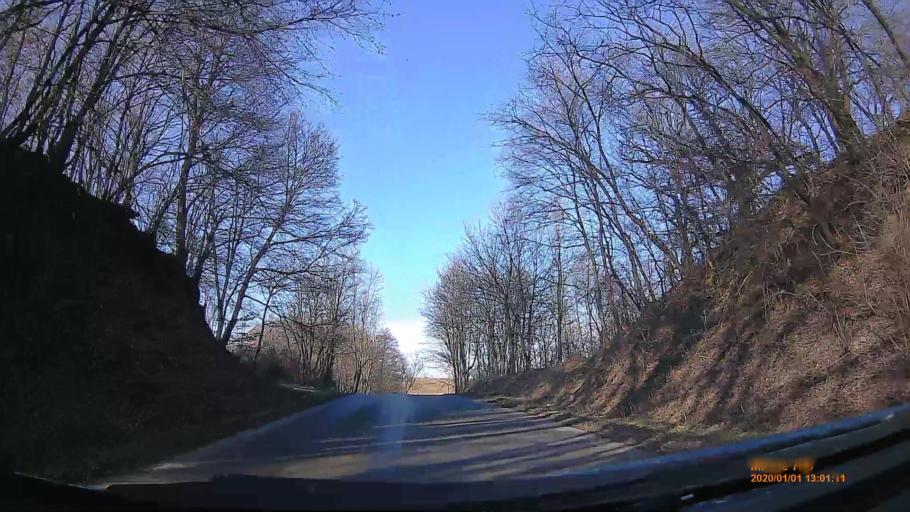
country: HU
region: Heves
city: Parad
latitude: 47.9276
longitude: 20.0226
